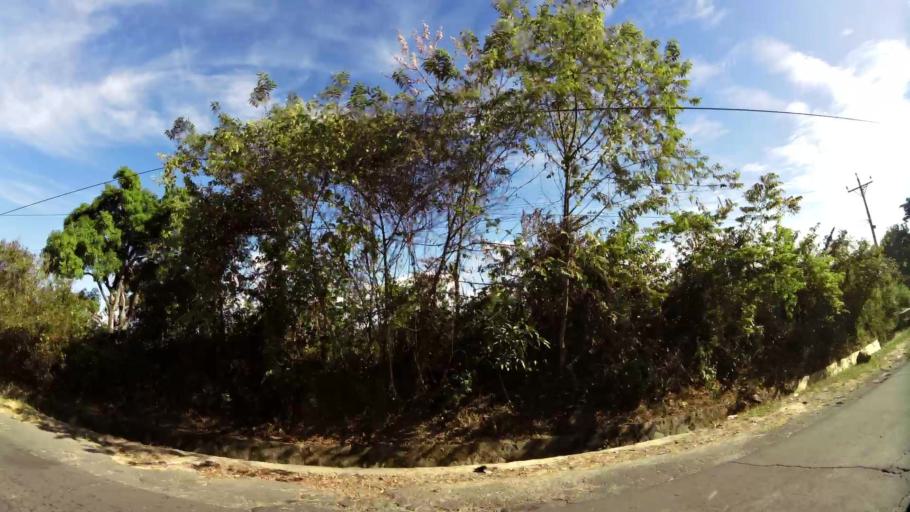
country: SV
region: Cuscatlan
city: Tenancingo
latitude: 13.8304
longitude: -89.0313
